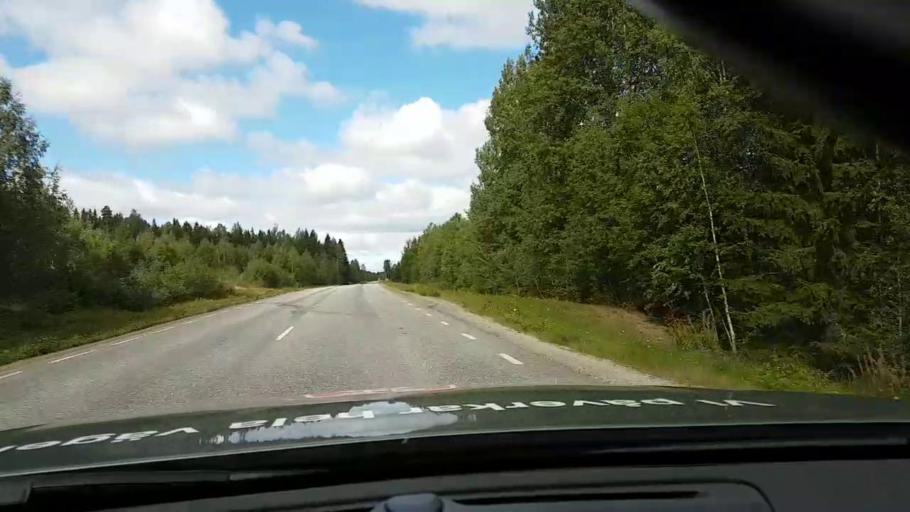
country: SE
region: Vaesternorrland
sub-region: OErnskoeldsviks Kommun
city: Bredbyn
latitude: 63.4724
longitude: 18.0981
